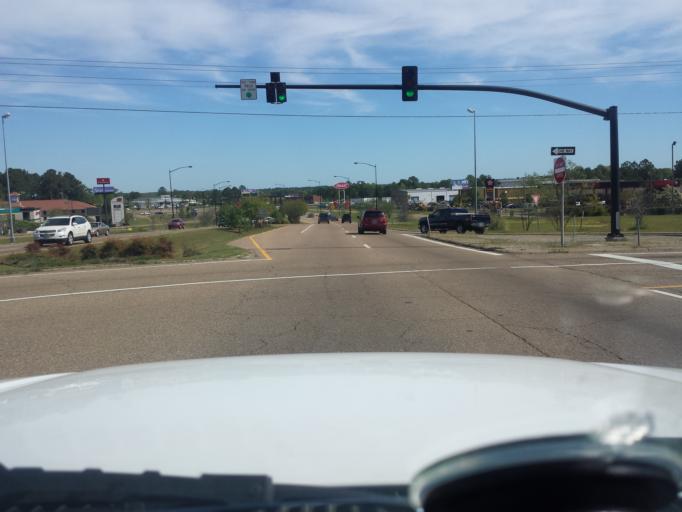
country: US
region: Mississippi
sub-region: Rankin County
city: Pearl
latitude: 32.2726
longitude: -90.0728
